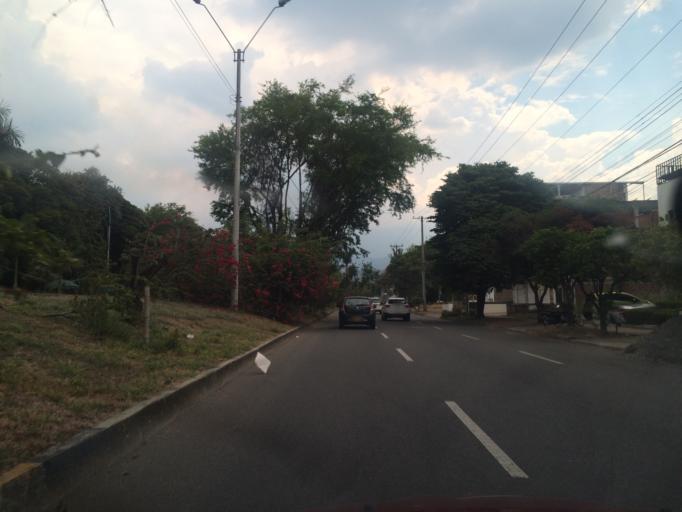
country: CO
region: Valle del Cauca
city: Cali
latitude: 3.3878
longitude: -76.5299
